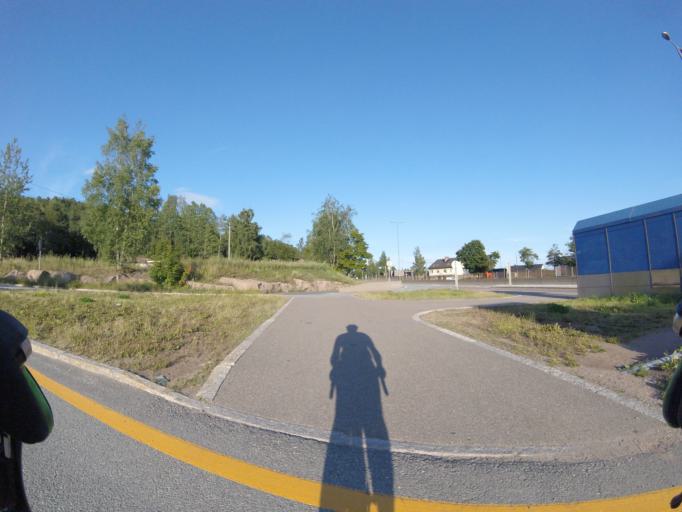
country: NO
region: Akershus
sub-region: Lorenskog
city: Kjenn
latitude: 59.9600
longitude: 10.8854
